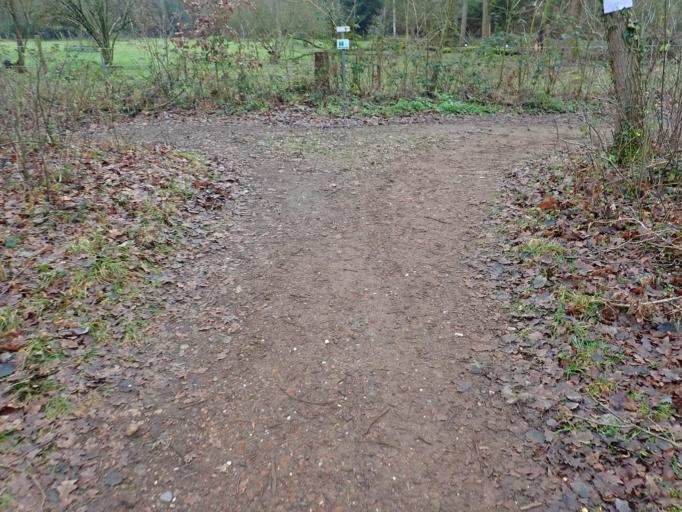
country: BE
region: Flanders
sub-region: Provincie Antwerpen
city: Schilde
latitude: 51.2163
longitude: 4.6147
